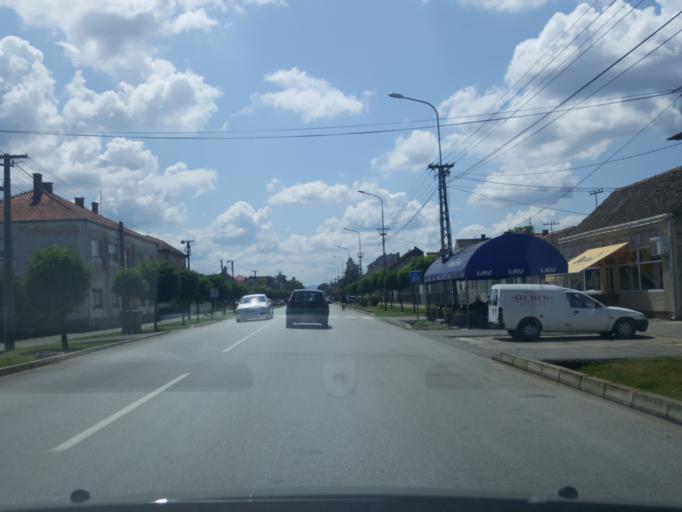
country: RS
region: Central Serbia
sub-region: Macvanski Okrug
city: Bogatic
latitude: 44.8400
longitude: 19.4810
